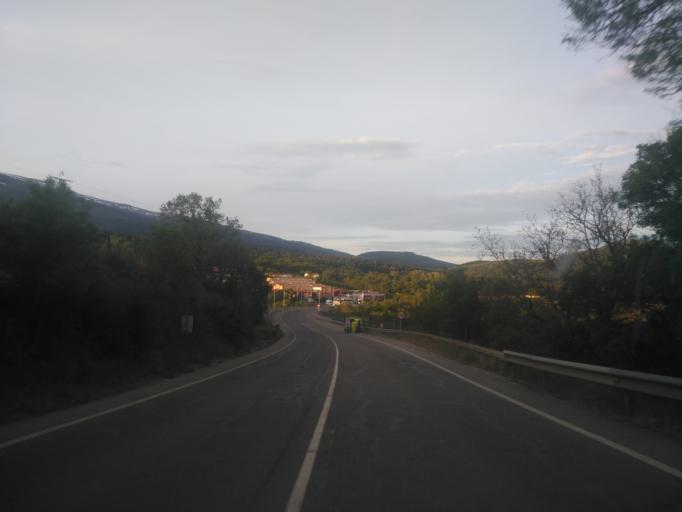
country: ES
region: Castille and Leon
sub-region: Provincia de Salamanca
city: Bejar
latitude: 40.3940
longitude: -5.7400
